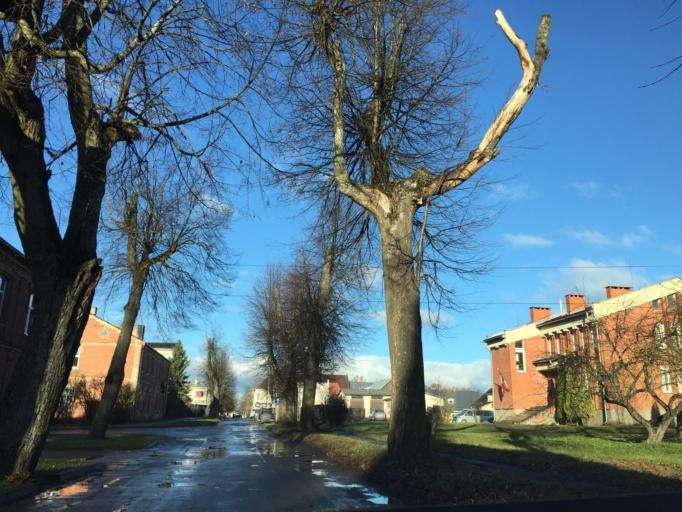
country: LV
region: Valmieras Rajons
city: Valmiera
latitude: 57.5359
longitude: 25.4125
